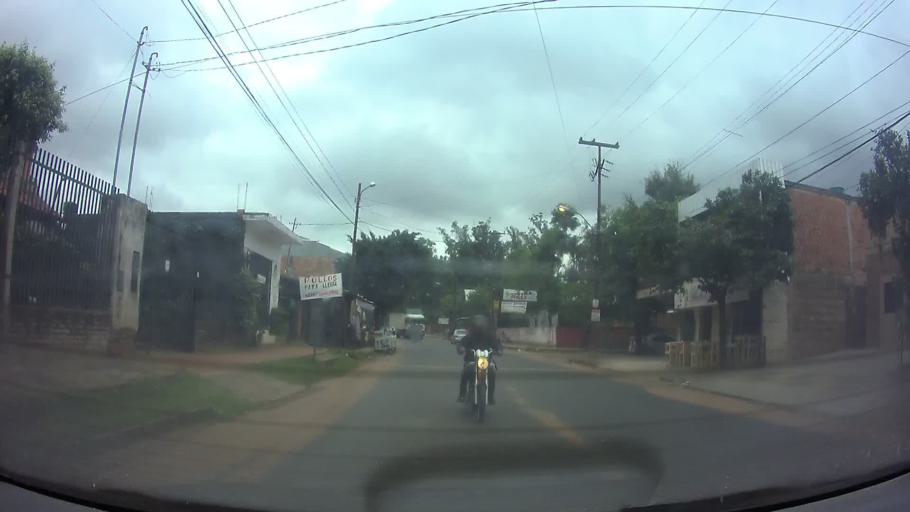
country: PY
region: Central
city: Nemby
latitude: -25.3843
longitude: -57.5479
